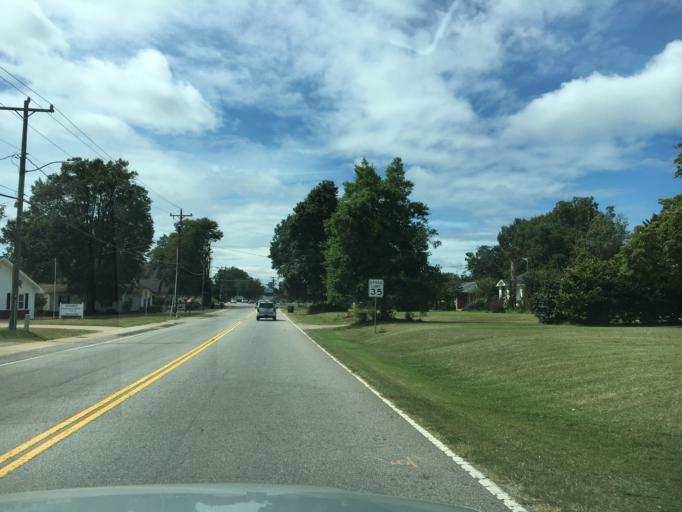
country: US
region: South Carolina
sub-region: Spartanburg County
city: Duncan
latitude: 34.9354
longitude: -82.1338
